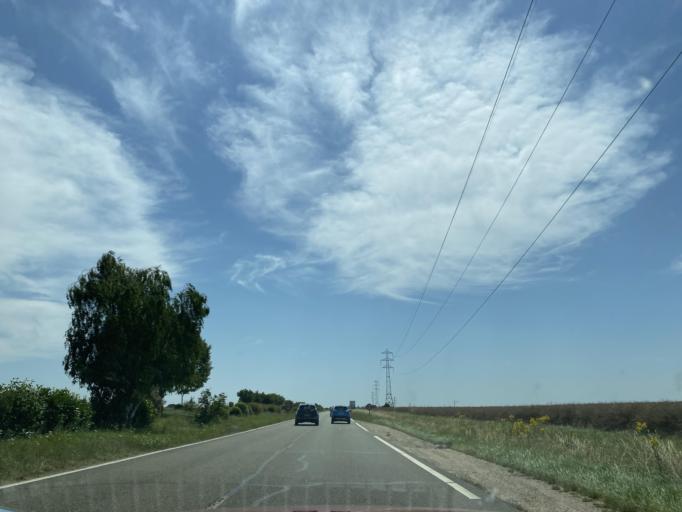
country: FR
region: Centre
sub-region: Departement d'Eure-et-Loir
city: Leves
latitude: 48.4661
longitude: 1.4645
